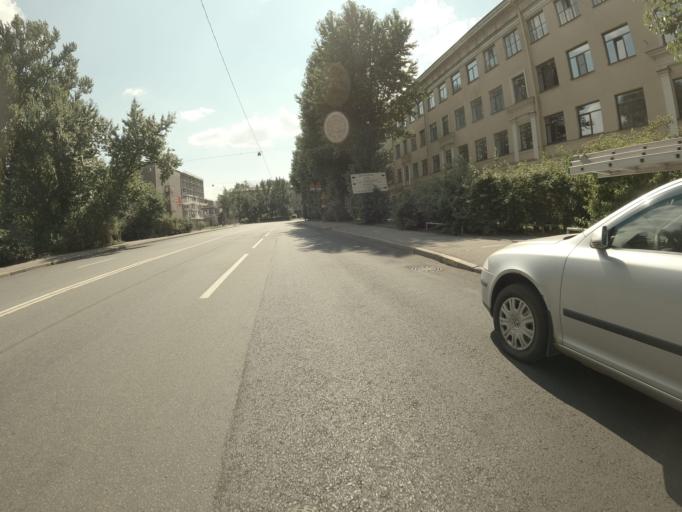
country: RU
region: St.-Petersburg
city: Vasyl'evsky Ostrov
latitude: 59.9100
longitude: 30.2516
